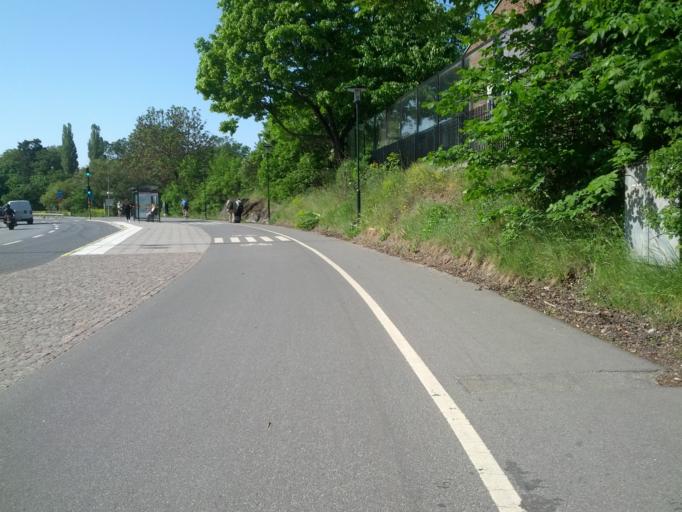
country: SE
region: Stockholm
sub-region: Stockholms Kommun
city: Stockholm
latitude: 59.3605
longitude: 18.0558
